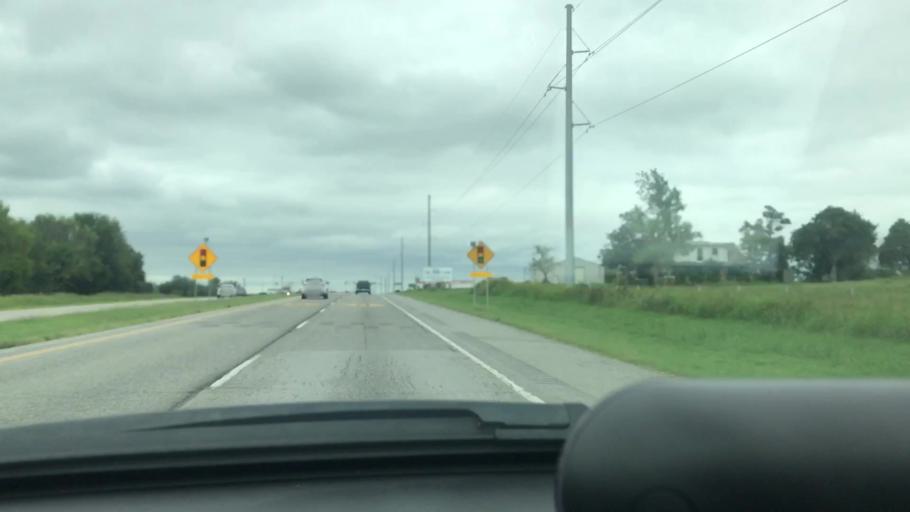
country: US
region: Oklahoma
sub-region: Wagoner County
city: Wagoner
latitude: 36.0140
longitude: -95.3687
